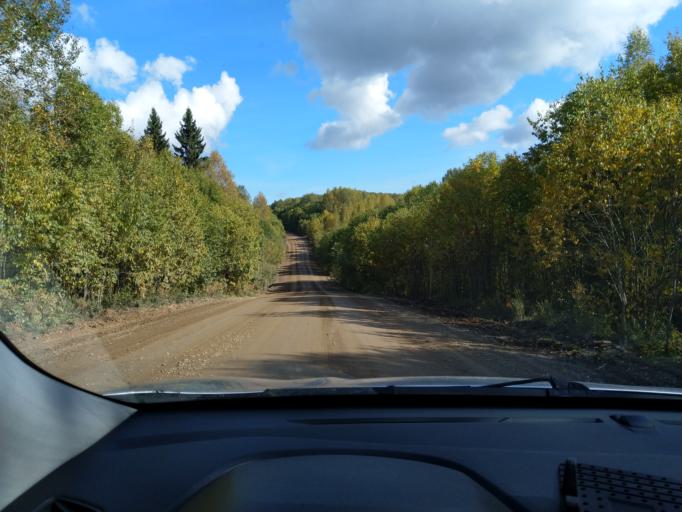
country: RU
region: Perm
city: Pozhva
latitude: 59.4217
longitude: 56.2649
